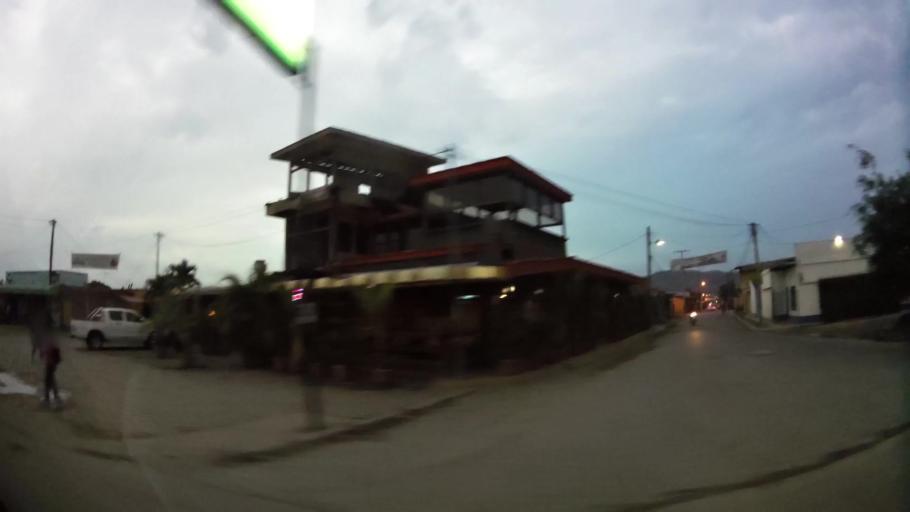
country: NI
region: Esteli
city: Esteli
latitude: 13.1022
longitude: -86.3523
